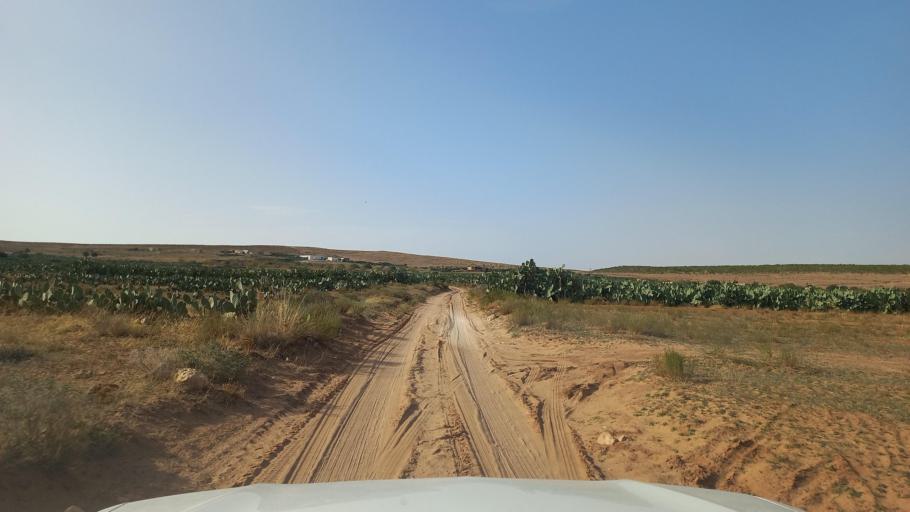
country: TN
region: Al Qasrayn
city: Kasserine
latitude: 35.3588
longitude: 8.8523
